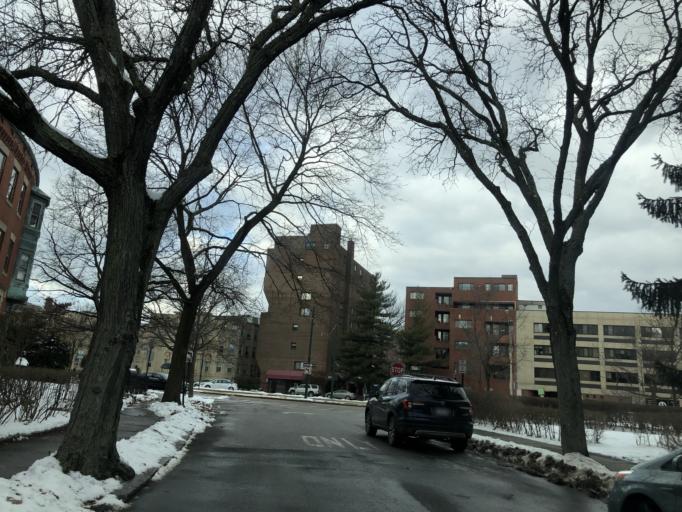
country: US
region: Massachusetts
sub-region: Norfolk County
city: Brookline
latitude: 42.3365
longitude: -71.1452
